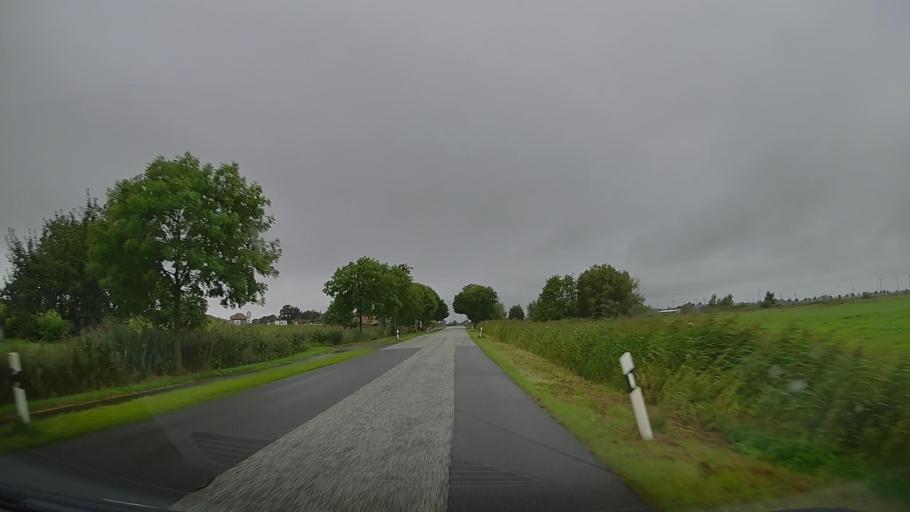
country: DE
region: Schleswig-Holstein
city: Sankt Margarethen
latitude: 53.8778
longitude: 9.2785
